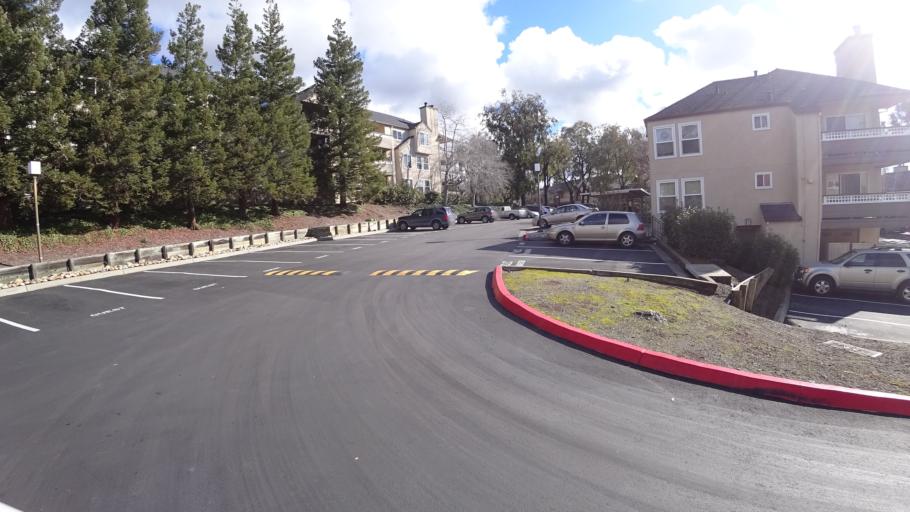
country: US
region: California
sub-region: Alameda County
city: Fairview
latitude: 37.6334
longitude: -122.0457
